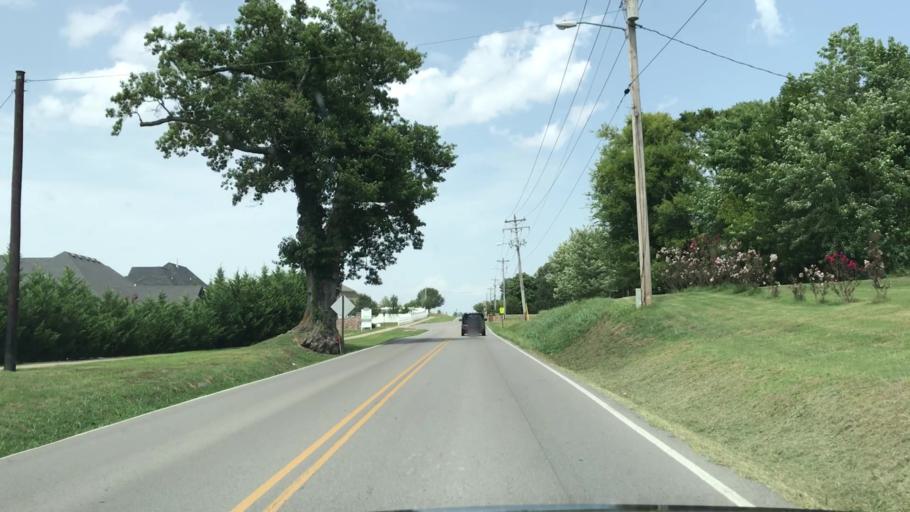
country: US
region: Tennessee
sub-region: Rutherford County
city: La Vergne
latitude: 35.9592
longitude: -86.6004
